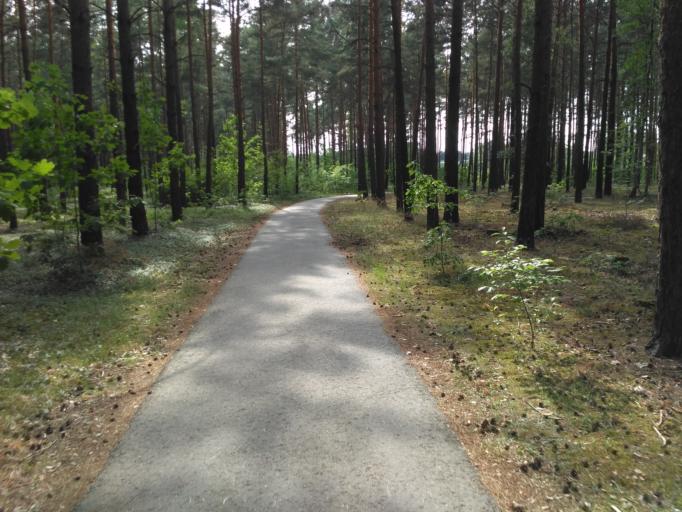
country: DE
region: Saxony
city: Hoyerswerda
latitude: 51.4447
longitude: 14.2890
